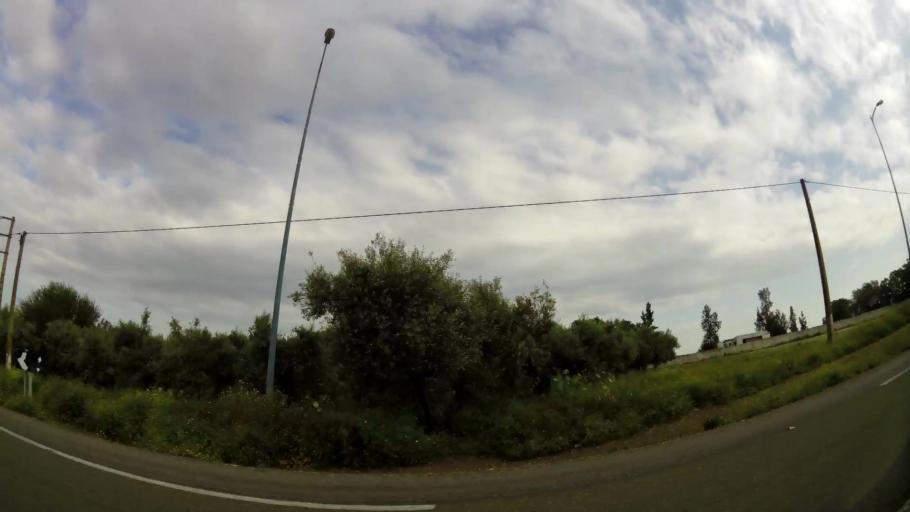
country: MA
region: Rabat-Sale-Zemmour-Zaer
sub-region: Khemisset
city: Khemisset
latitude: 33.7851
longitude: -6.1267
